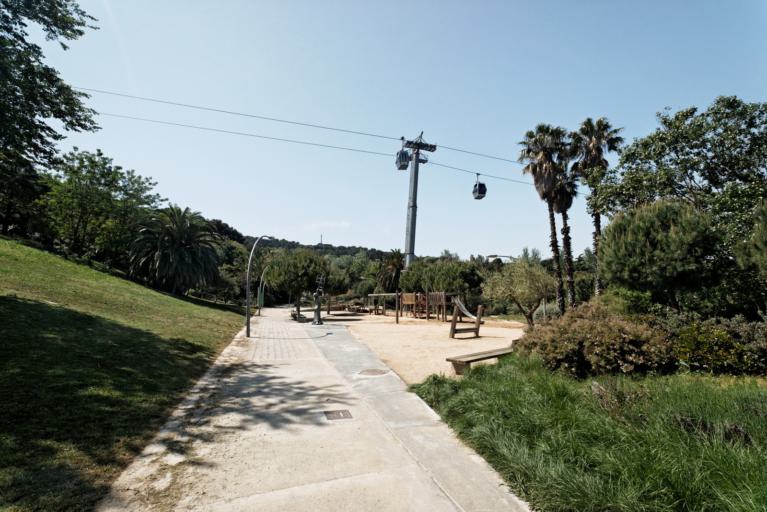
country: ES
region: Catalonia
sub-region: Provincia de Barcelona
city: Sants-Montjuic
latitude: 41.3685
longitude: 2.1662
